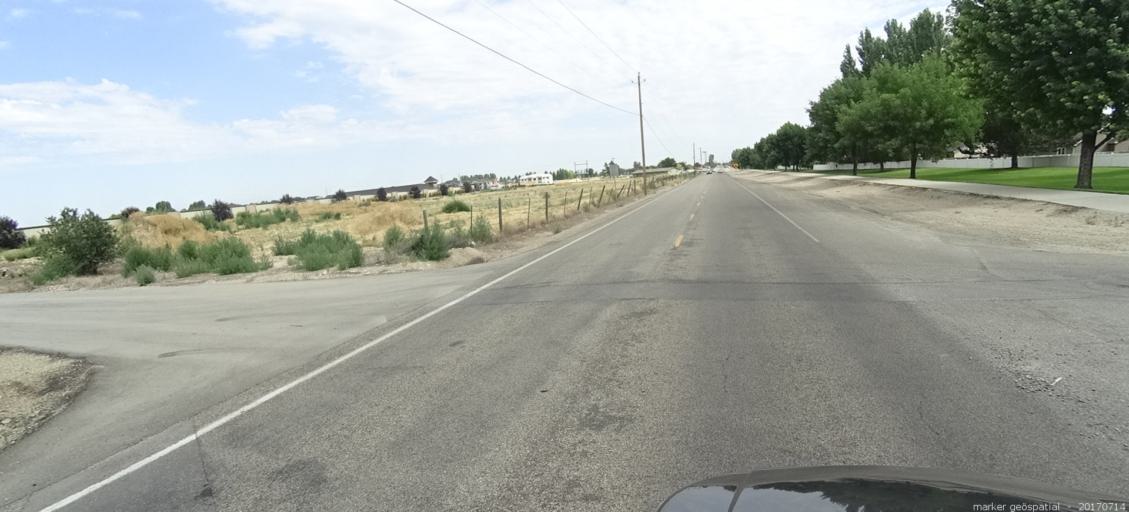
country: US
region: Idaho
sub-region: Ada County
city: Kuna
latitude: 43.5001
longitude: -116.4336
